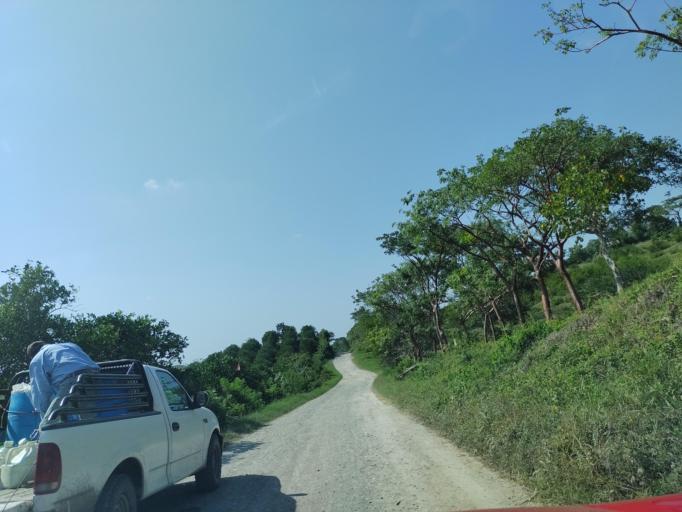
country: MX
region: Puebla
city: San Jose Acateno
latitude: 20.2558
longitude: -97.2119
